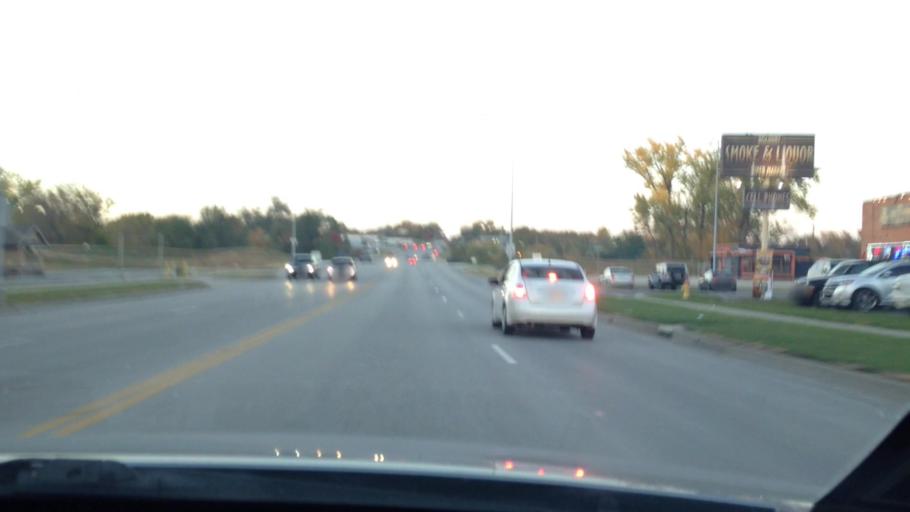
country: US
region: Missouri
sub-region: Platte County
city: Riverside
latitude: 39.1737
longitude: -94.6128
